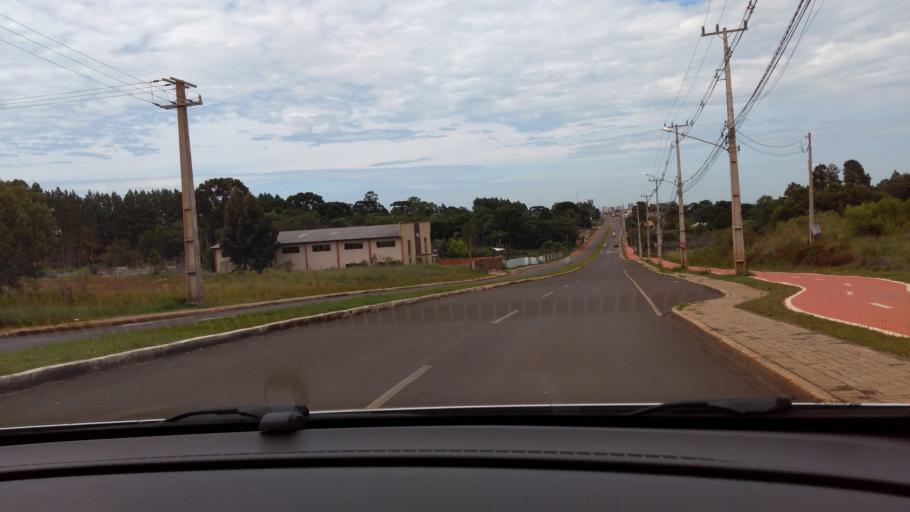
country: BR
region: Parana
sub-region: Guarapuava
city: Guarapuava
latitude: -25.3676
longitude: -51.4368
